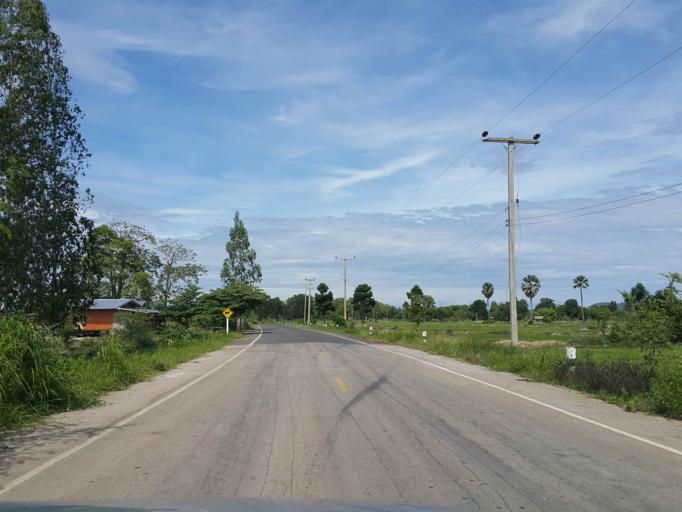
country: TH
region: Sukhothai
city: Ban Dan Lan Hoi
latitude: 17.1158
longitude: 99.5325
